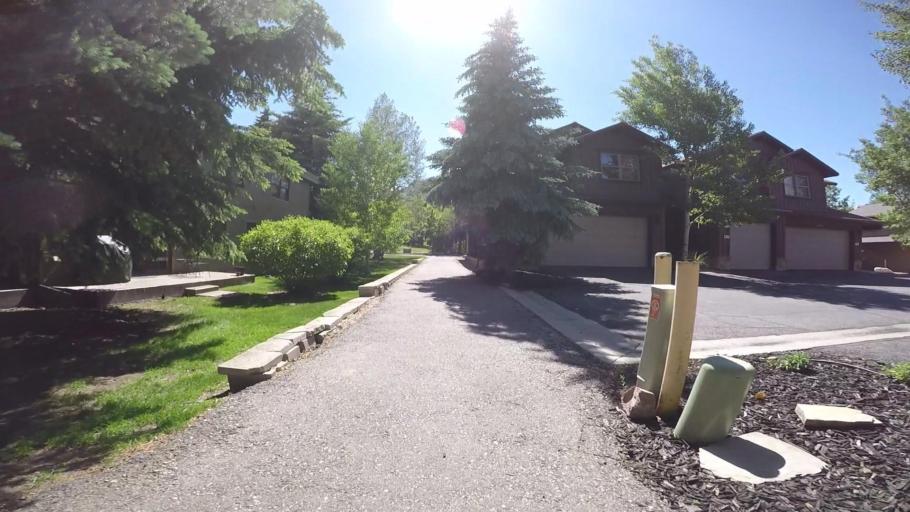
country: US
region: Utah
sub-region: Summit County
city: Park City
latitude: 40.6660
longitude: -111.5126
